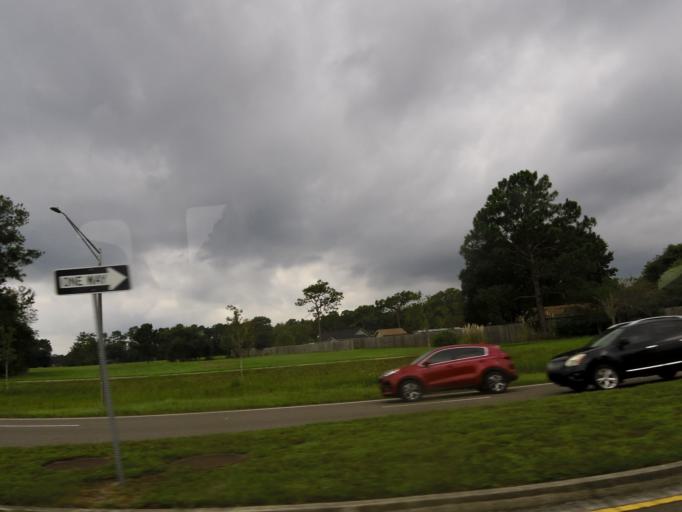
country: US
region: Florida
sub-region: Clay County
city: Bellair-Meadowbrook Terrace
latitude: 30.1987
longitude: -81.7978
